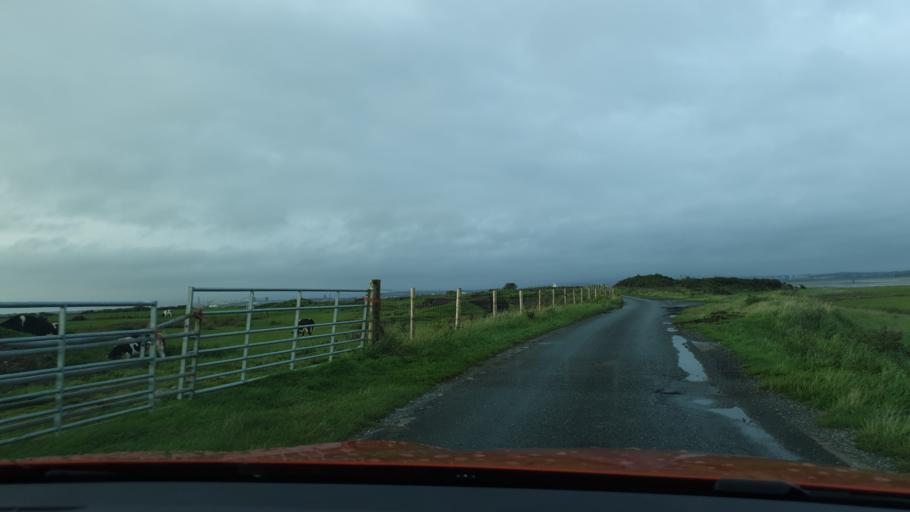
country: GB
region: England
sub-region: Cumbria
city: Barrow in Furness
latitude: 54.0637
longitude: -3.2112
